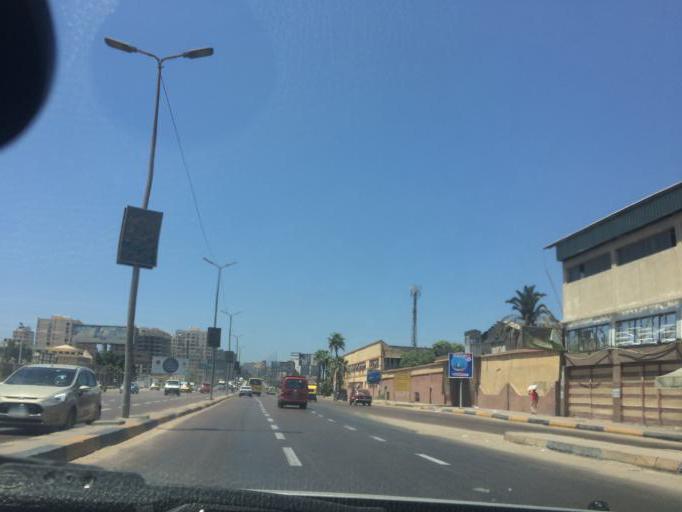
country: EG
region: Alexandria
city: Alexandria
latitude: 31.1825
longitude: 29.9273
